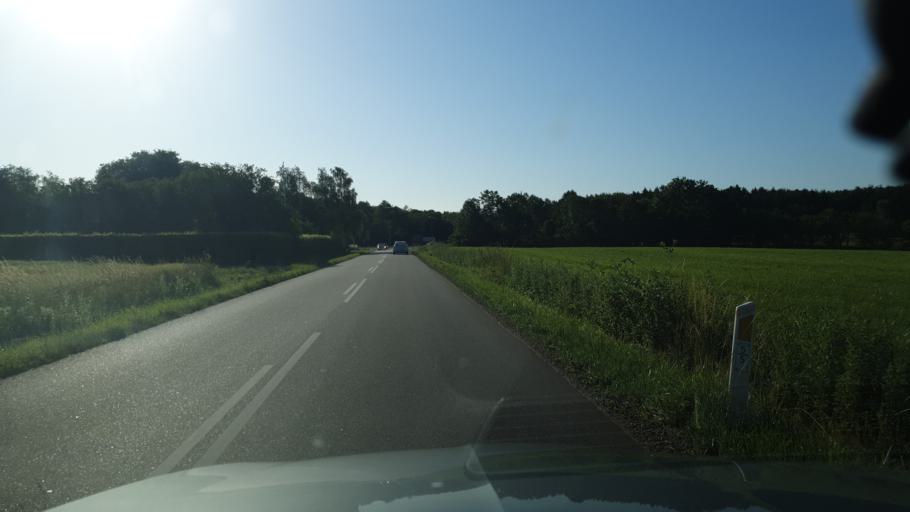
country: DK
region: Zealand
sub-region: Soro Kommune
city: Frederiksberg
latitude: 55.4078
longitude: 11.6189
